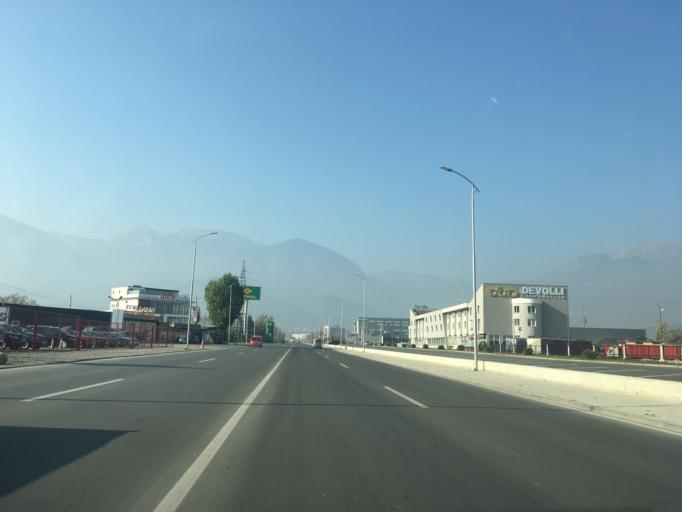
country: XK
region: Pec
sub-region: Komuna e Pejes
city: Peje
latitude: 42.6566
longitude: 20.3252
